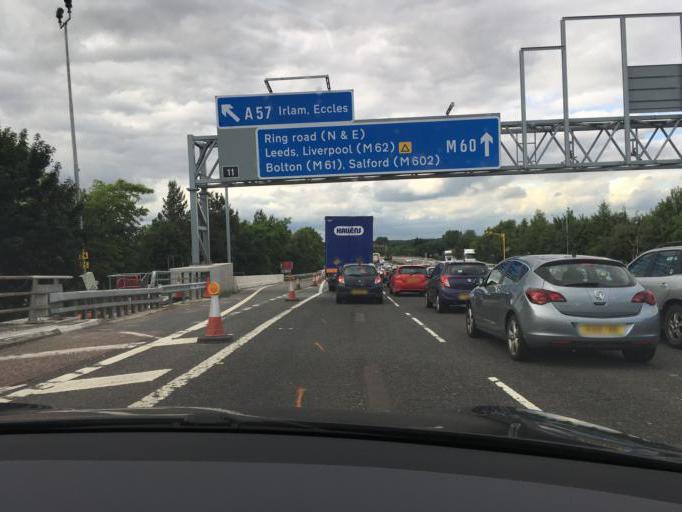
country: GB
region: England
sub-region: Trafford
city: Urmston
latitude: 53.4728
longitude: -2.3722
